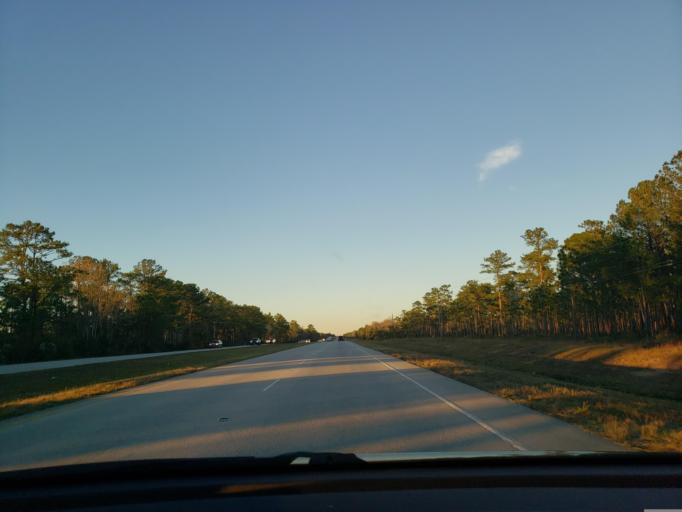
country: US
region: North Carolina
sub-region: Onslow County
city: Sneads Ferry
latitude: 34.6222
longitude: -77.4831
